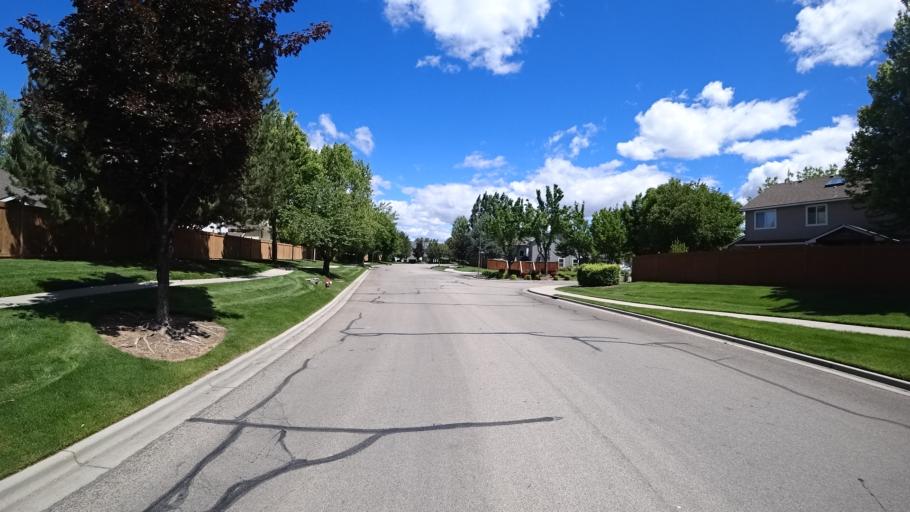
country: US
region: Idaho
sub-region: Ada County
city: Meridian
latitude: 43.6417
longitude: -116.3487
